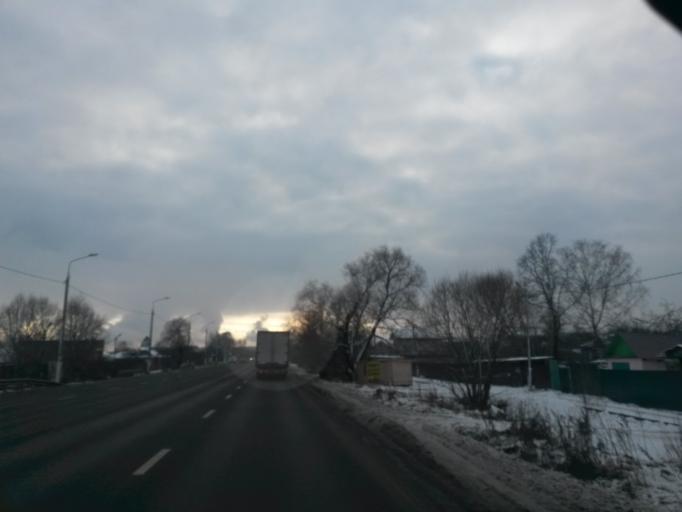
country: RU
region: Moskovskaya
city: Klimovsk
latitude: 55.3516
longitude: 37.5298
